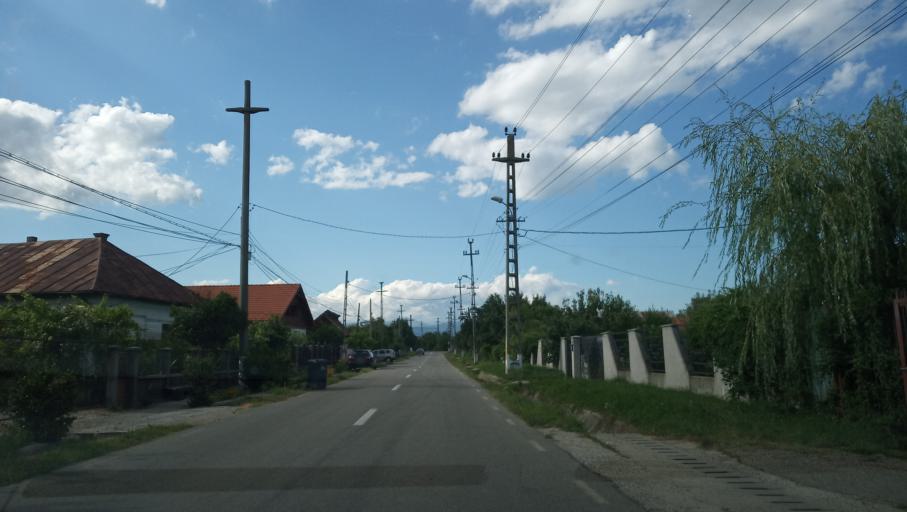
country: RO
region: Gorj
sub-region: Comuna Turcinesti
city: Turcinesti
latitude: 45.0658
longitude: 23.3473
